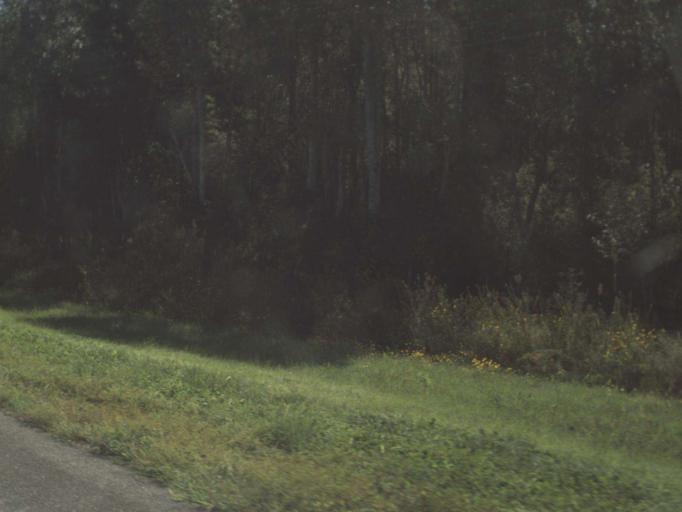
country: US
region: Florida
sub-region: Jefferson County
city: Monticello
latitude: 30.5055
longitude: -83.7660
